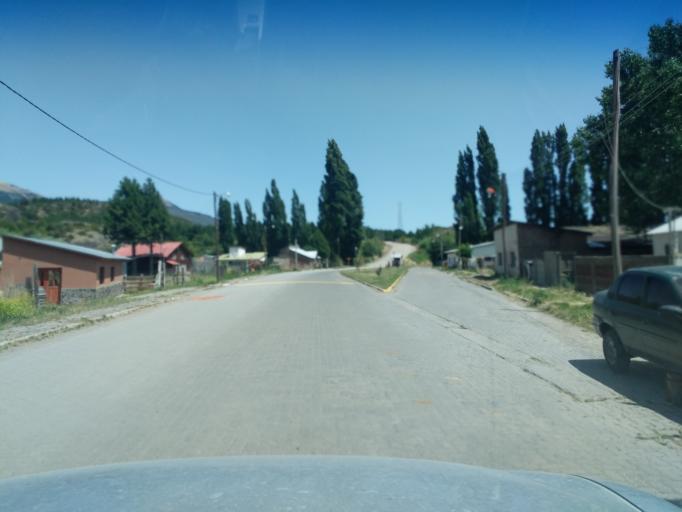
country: CL
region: Los Lagos
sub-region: Provincia de Palena
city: Palena
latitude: -43.5366
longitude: -71.4748
